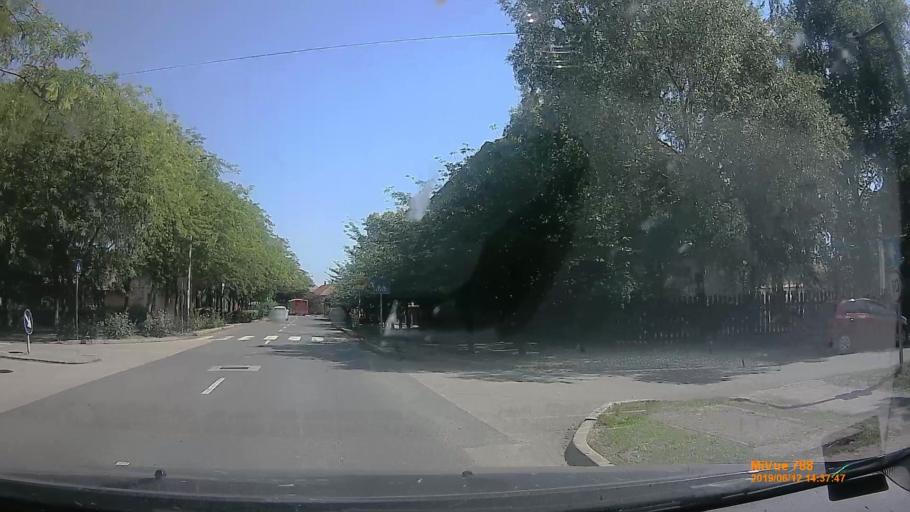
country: HU
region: Csongrad
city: Mako
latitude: 46.2117
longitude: 20.4739
